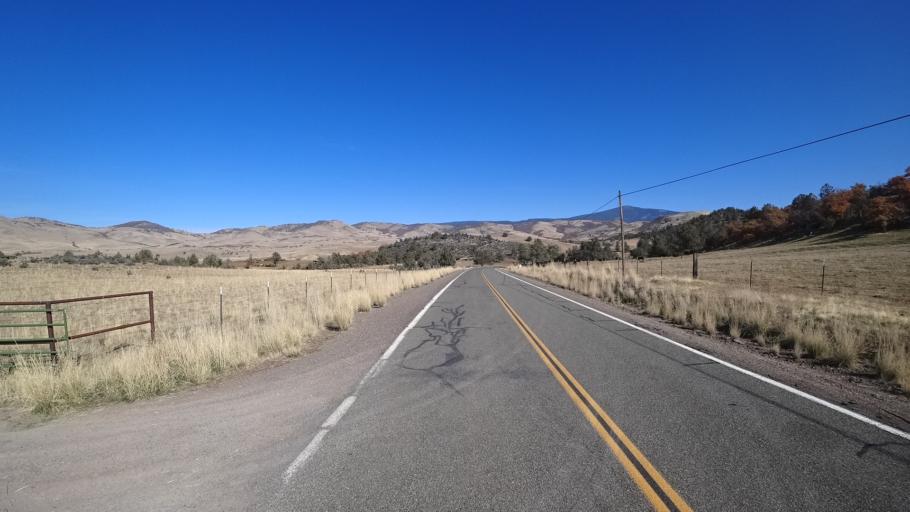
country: US
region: California
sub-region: Siskiyou County
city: Montague
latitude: 41.8070
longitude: -122.3887
